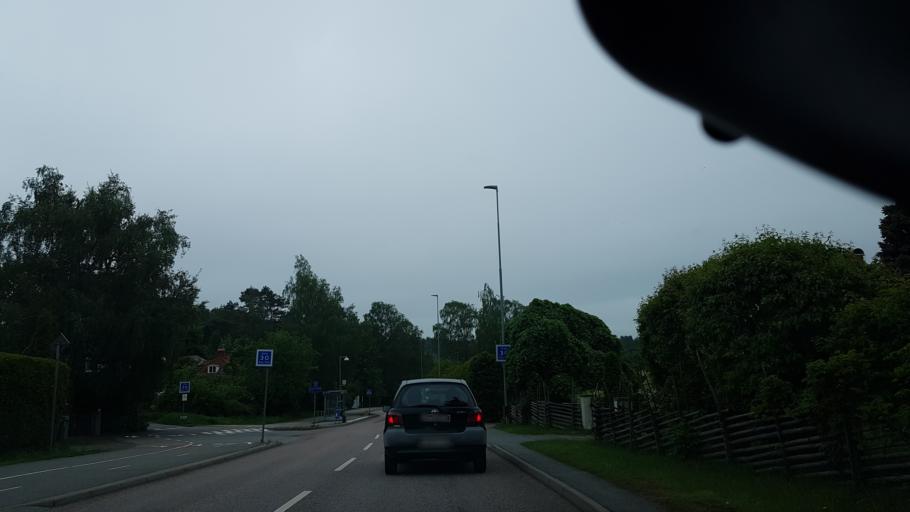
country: SE
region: Vaestra Goetaland
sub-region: Goteborg
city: Billdal
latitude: 57.6227
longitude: 11.9460
